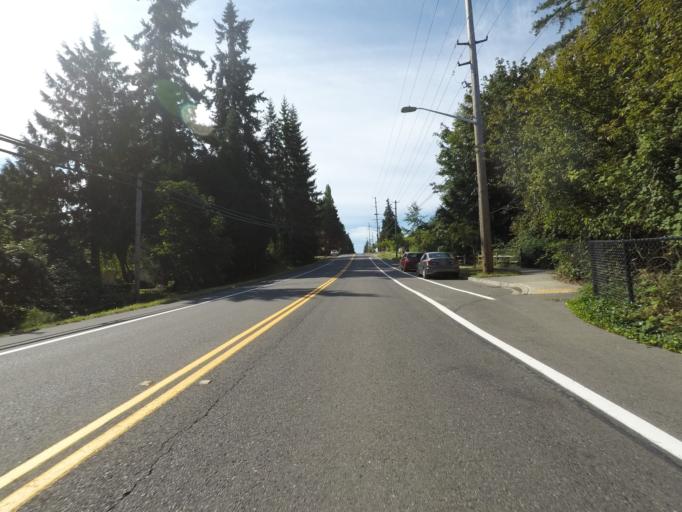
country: US
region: Washington
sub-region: King County
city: Inglewood-Finn Hill
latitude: 47.7216
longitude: -122.2294
